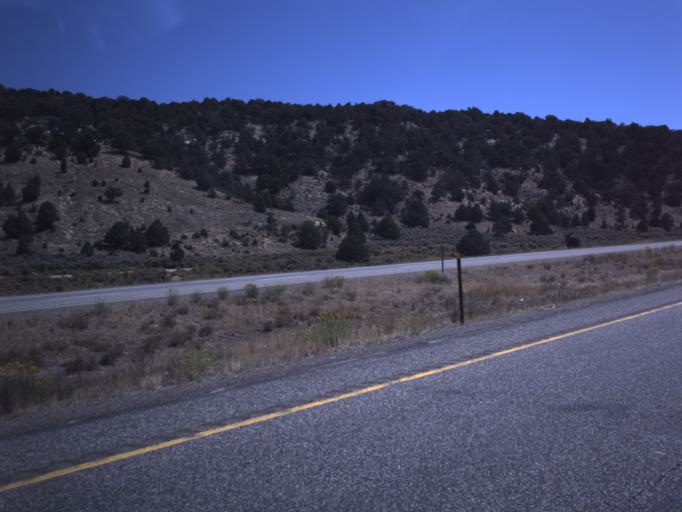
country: US
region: Utah
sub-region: Sevier County
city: Salina
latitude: 38.8086
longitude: -111.5327
